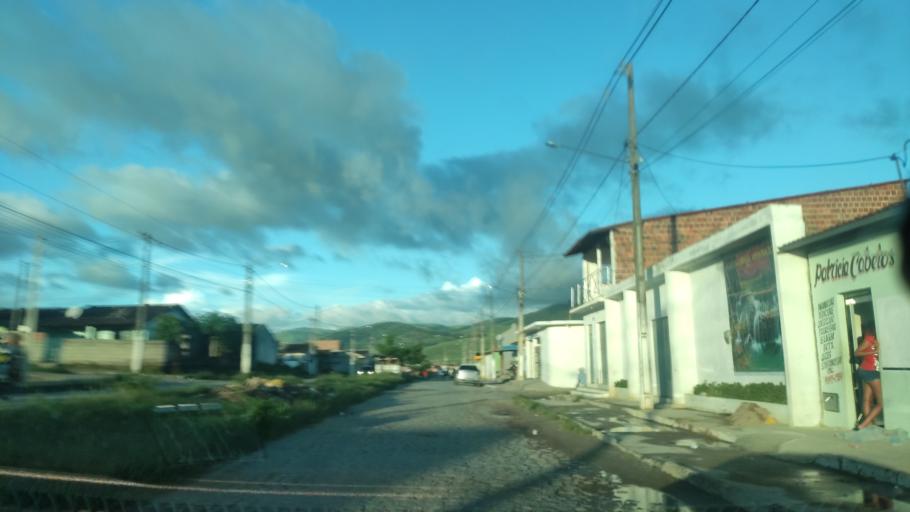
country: BR
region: Alagoas
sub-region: Uniao Dos Palmares
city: Uniao dos Palmares
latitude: -9.1512
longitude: -36.0112
